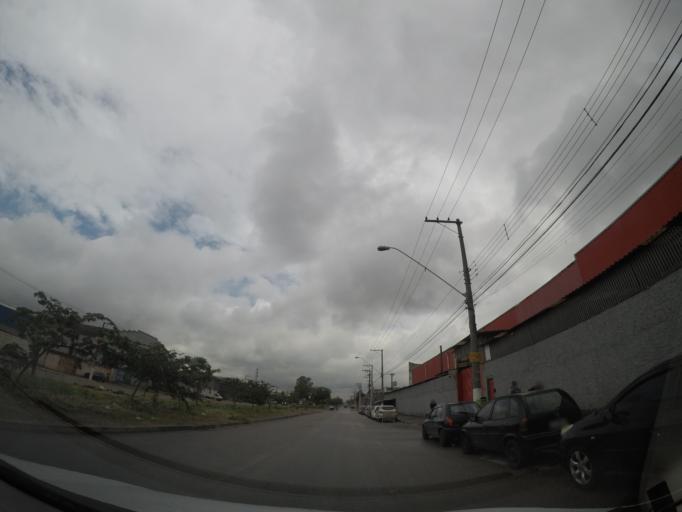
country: BR
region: Sao Paulo
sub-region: Guarulhos
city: Guarulhos
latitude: -23.4658
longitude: -46.4745
